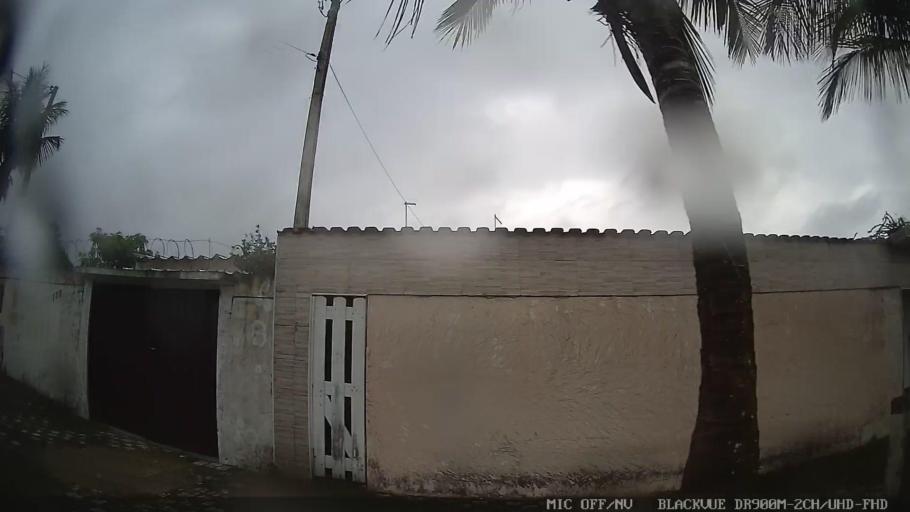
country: BR
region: Sao Paulo
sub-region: Itanhaem
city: Itanhaem
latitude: -24.1386
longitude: -46.7046
